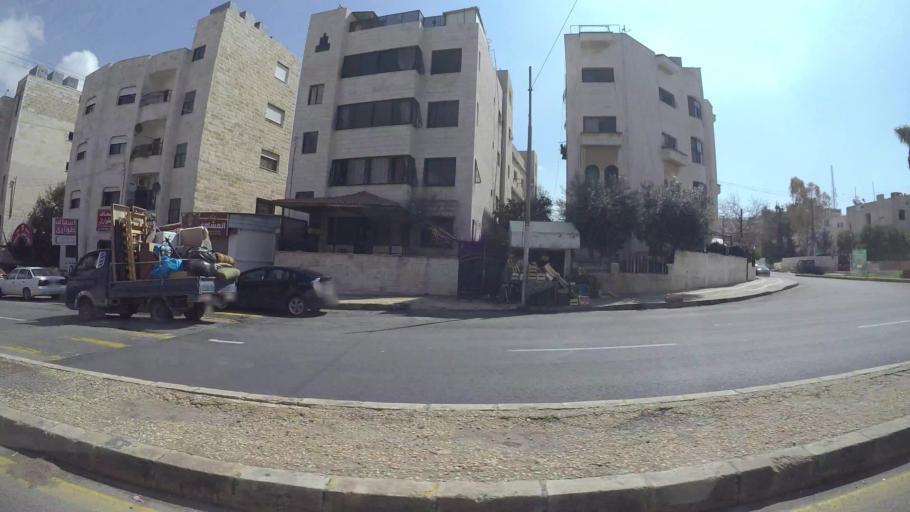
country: JO
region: Amman
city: Al Bunayyat ash Shamaliyah
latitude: 31.9292
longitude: 35.9026
